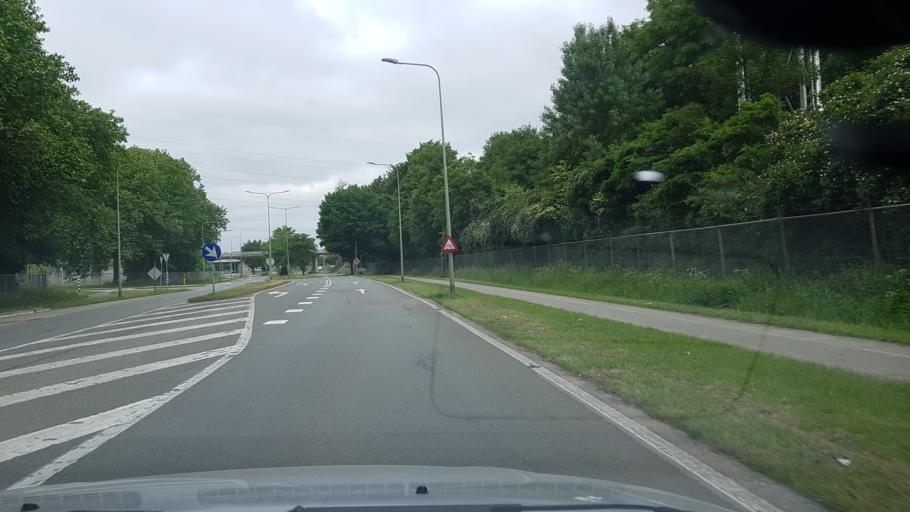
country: NL
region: Limburg
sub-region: Gemeente Stein
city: Urmond
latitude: 50.9743
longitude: 5.7931
